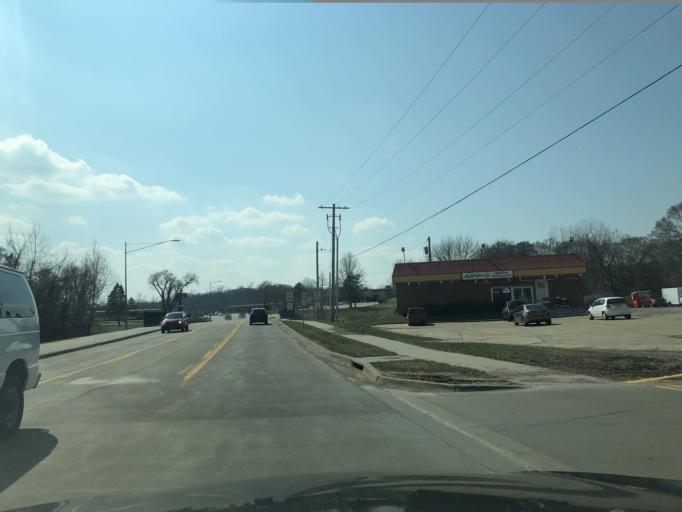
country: US
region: Missouri
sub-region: Platte County
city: Riverside
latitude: 39.1793
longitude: -94.6094
